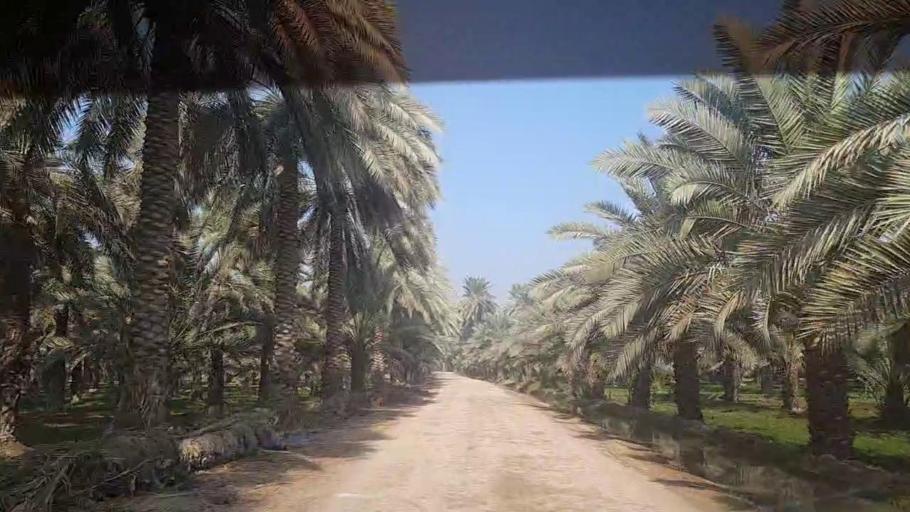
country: PK
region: Sindh
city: Khairpur
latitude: 27.4617
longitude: 68.7181
